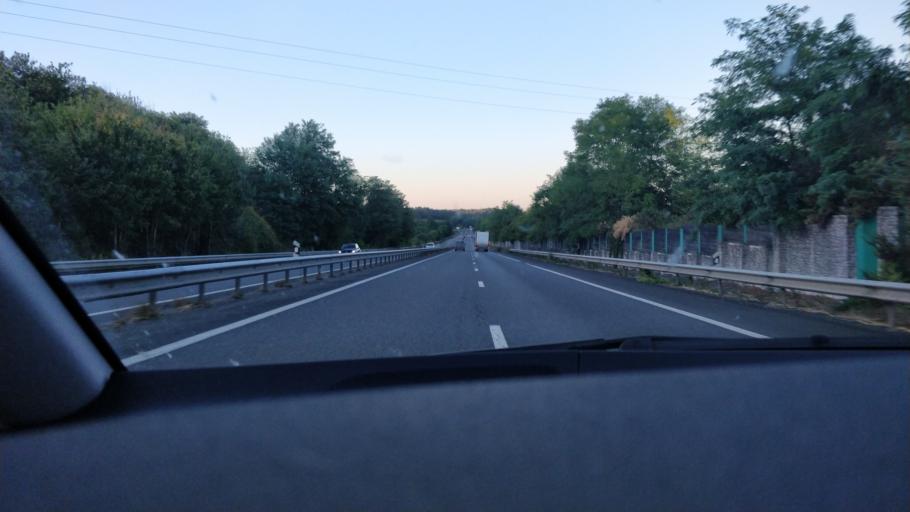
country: FR
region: Poitou-Charentes
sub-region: Departement de la Charente
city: Taponnat-Fleurignac
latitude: 45.7705
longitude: 0.4004
